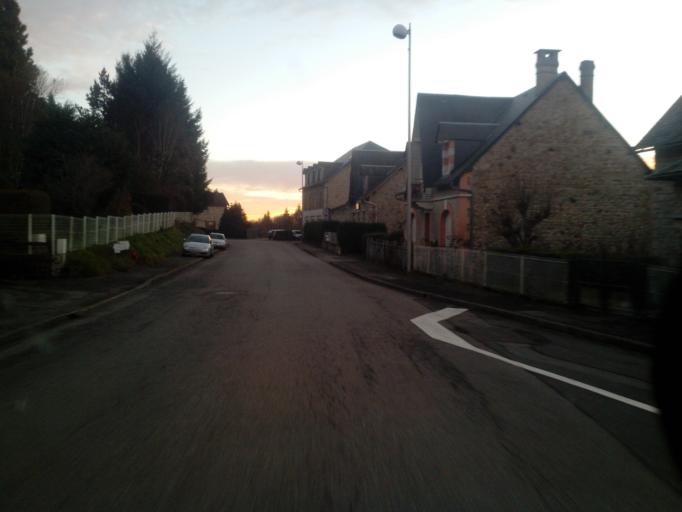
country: FR
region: Limousin
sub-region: Departement de la Correze
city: Meymac
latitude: 45.5386
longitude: 2.1411
